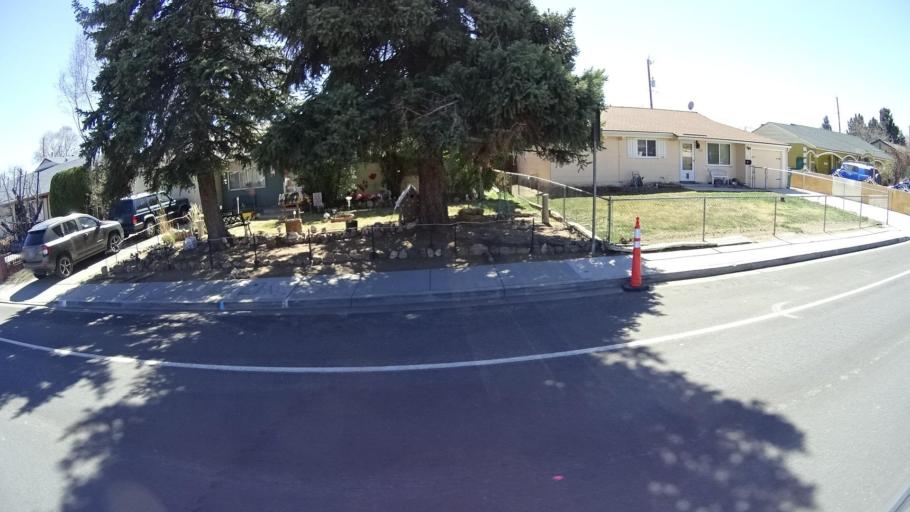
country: US
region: Nevada
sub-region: Washoe County
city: Sparks
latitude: 39.5530
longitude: -119.7604
